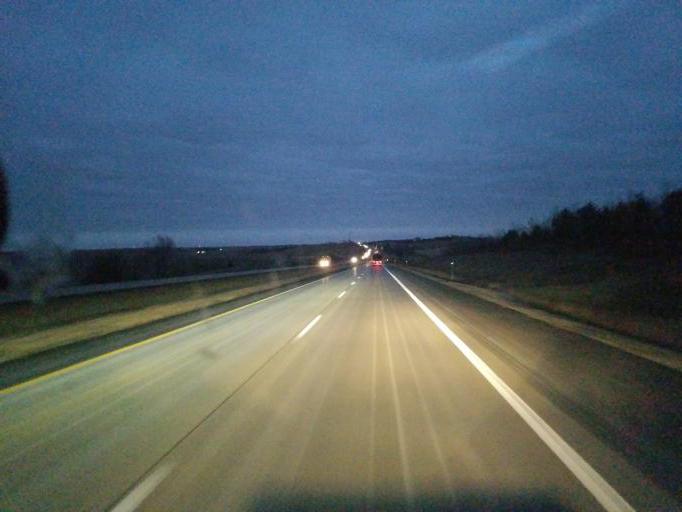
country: US
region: Iowa
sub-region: Cass County
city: Atlantic
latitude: 41.4967
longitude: -94.8062
